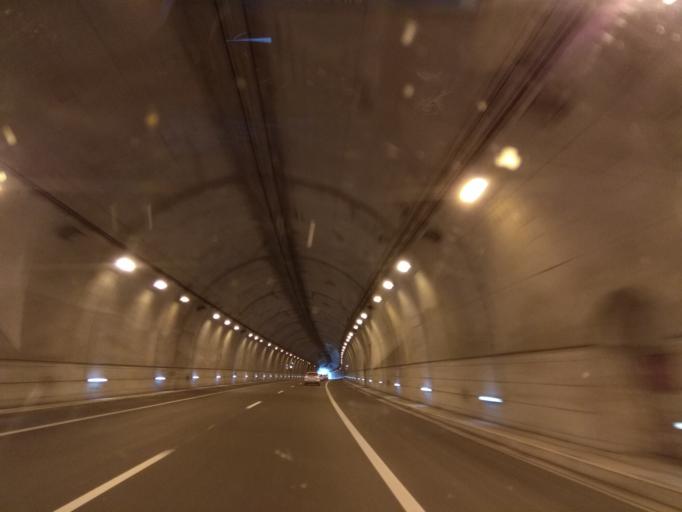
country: ES
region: Cantabria
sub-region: Provincia de Cantabria
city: Camargo
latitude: 43.3958
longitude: -3.8674
